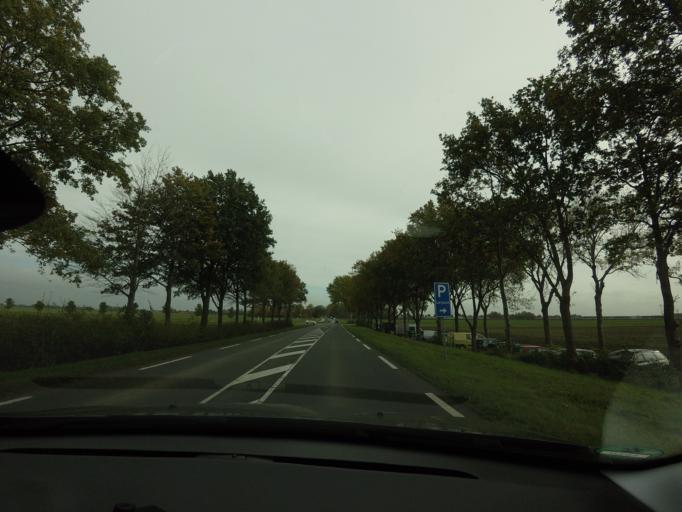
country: NL
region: Flevoland
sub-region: Gemeente Noordoostpolder
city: Emmeloord
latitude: 52.7255
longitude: 5.7761
